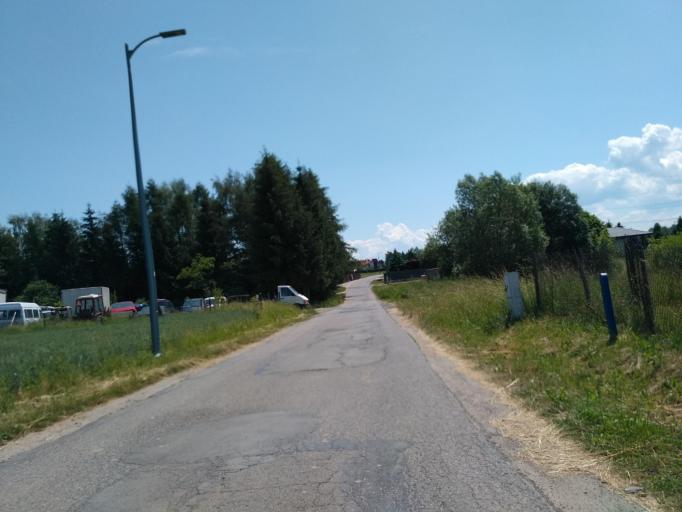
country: PL
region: Subcarpathian Voivodeship
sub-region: Powiat krosnienski
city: Korczyna
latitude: 49.7082
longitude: 21.7928
